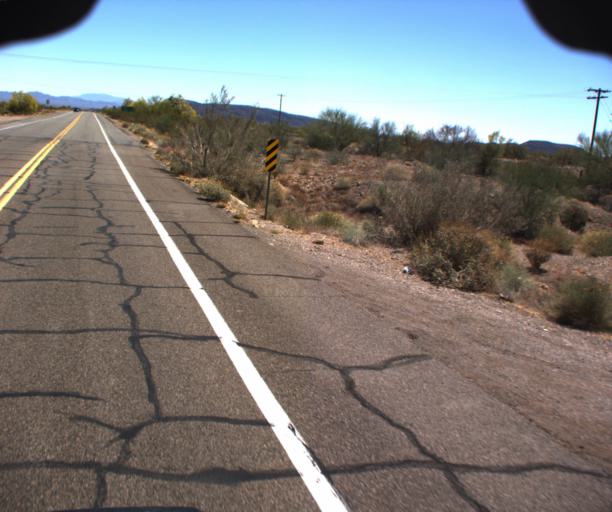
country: US
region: Arizona
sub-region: La Paz County
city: Quartzsite
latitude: 33.6645
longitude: -114.0068
